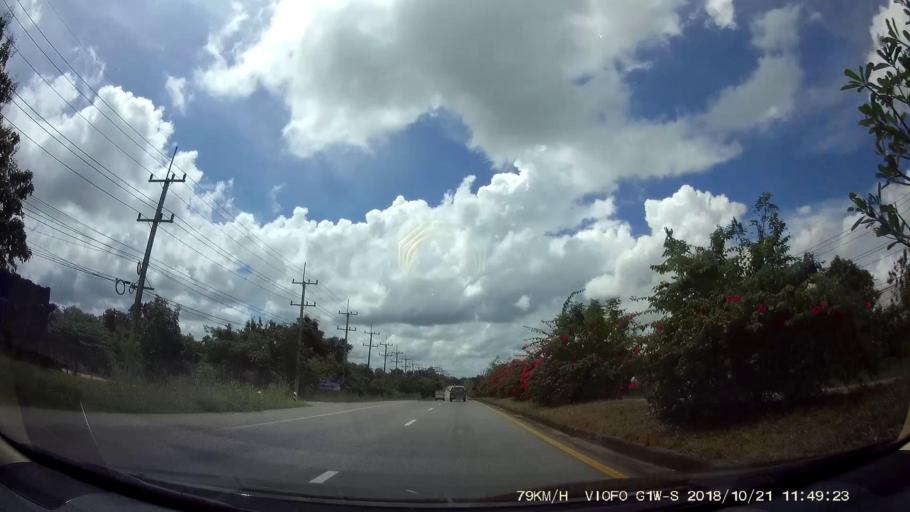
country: TH
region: Chaiyaphum
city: Noen Sa-nga
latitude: 15.6394
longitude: 101.9416
